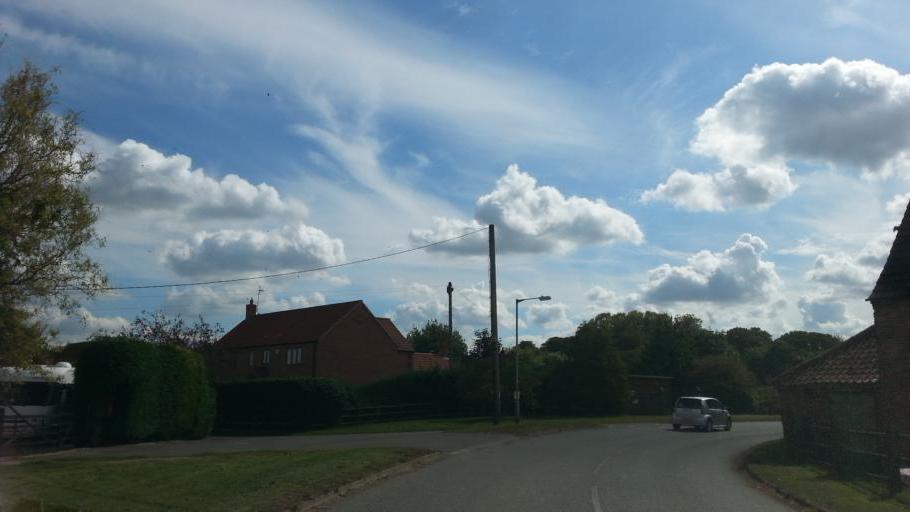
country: GB
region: England
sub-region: Nottinghamshire
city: Newark on Trent
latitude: 53.0942
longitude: -0.8454
